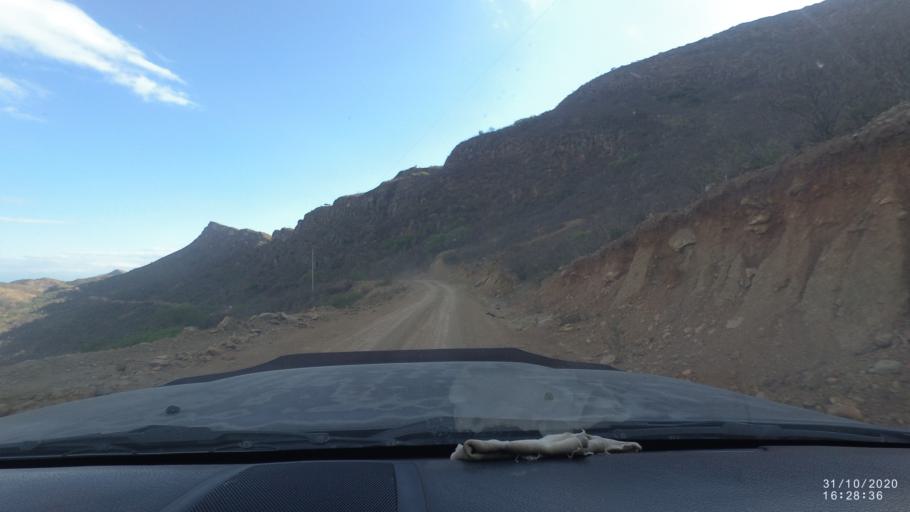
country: BO
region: Chuquisaca
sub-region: Provincia Zudanez
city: Mojocoya
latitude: -18.4137
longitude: -64.5867
